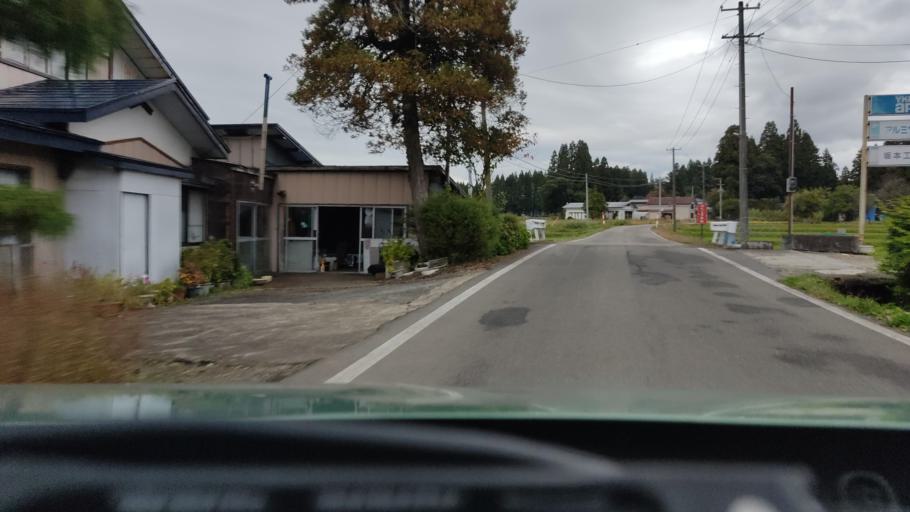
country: JP
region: Akita
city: Kakunodatemachi
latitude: 39.5681
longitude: 140.6113
